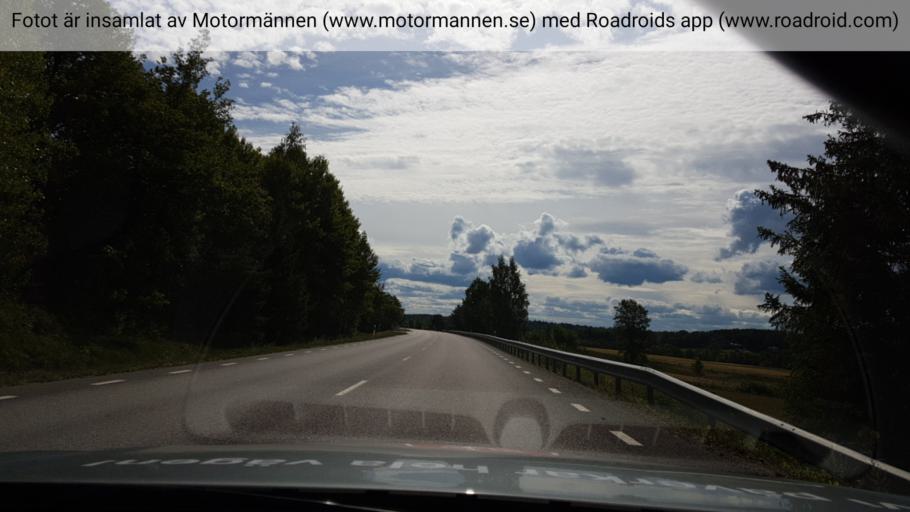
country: SE
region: Uppsala
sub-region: Osthammars Kommun
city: Bjorklinge
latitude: 59.9516
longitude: 17.4084
